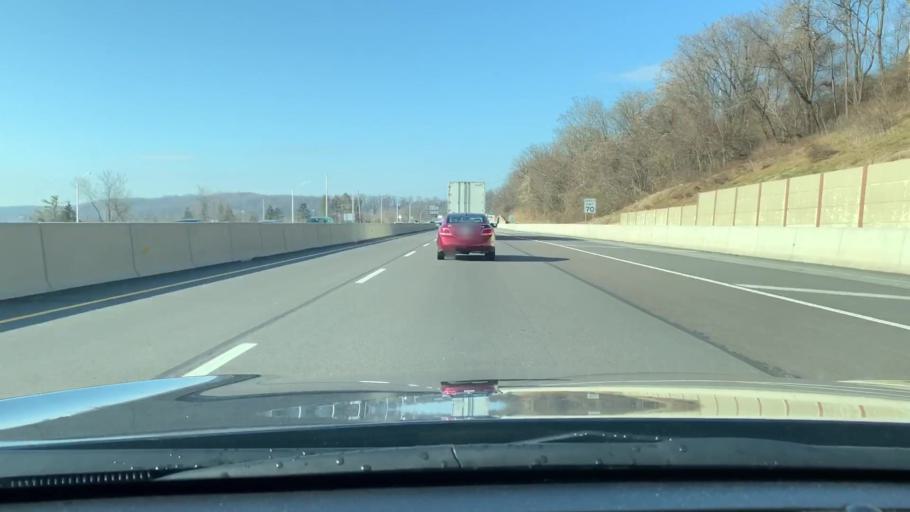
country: US
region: Pennsylvania
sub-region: Chester County
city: Malvern
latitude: 40.0754
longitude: -75.5321
